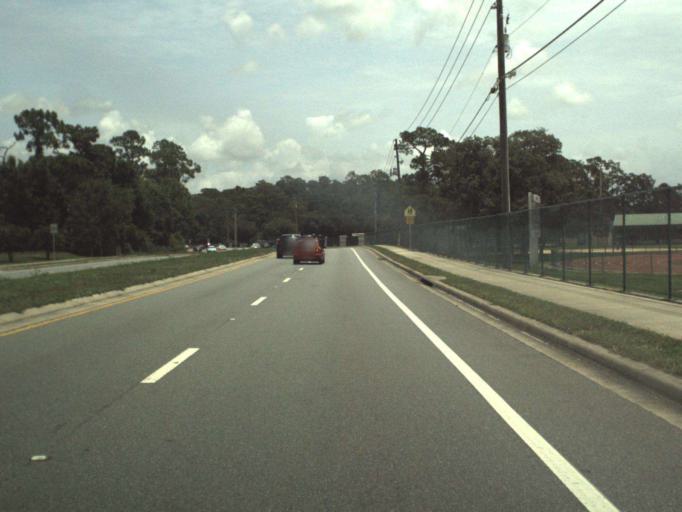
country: US
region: Florida
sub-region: Seminole County
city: Goldenrod
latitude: 28.6128
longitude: -81.2751
